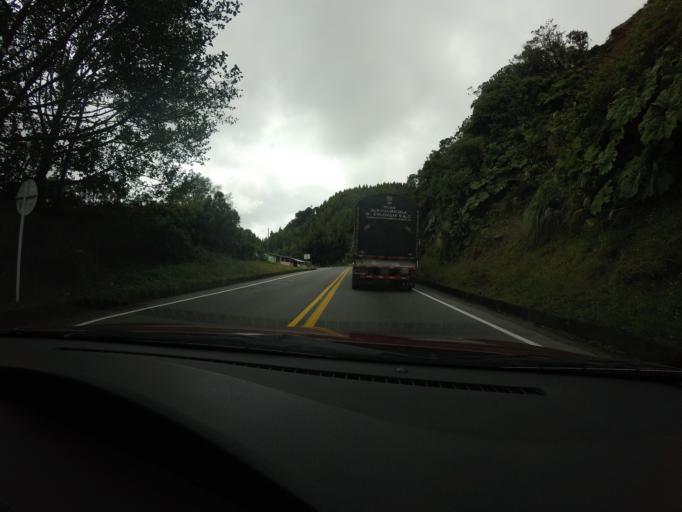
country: CO
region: Tolima
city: Herveo
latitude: 5.0597
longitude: -75.3152
